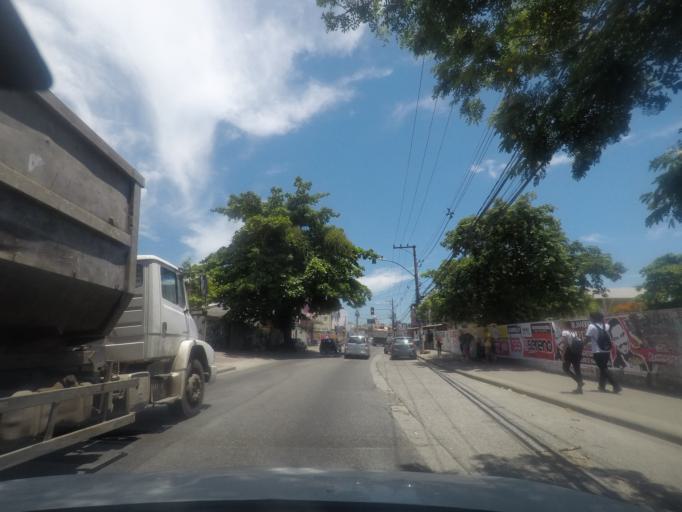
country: BR
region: Rio de Janeiro
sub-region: Itaguai
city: Itaguai
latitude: -22.9131
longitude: -43.6872
